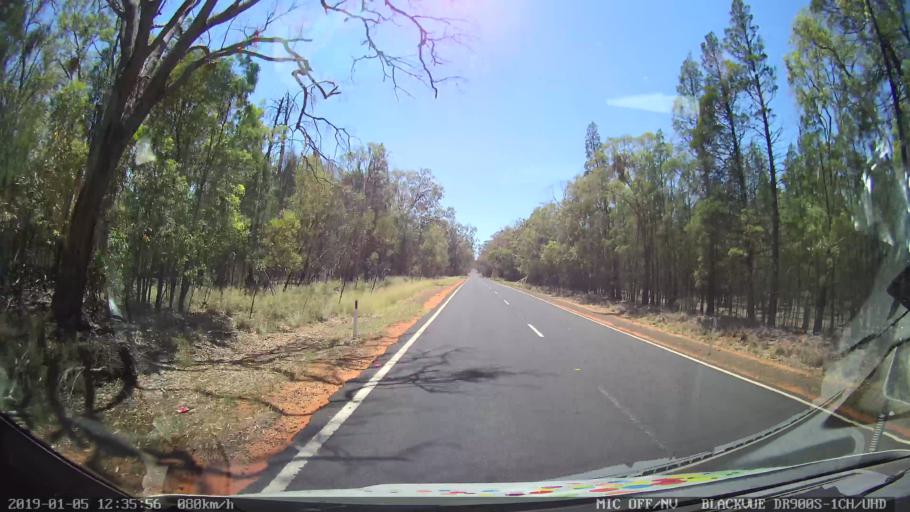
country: AU
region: New South Wales
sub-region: Warrumbungle Shire
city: Coonabarabran
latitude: -31.2084
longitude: 149.4330
